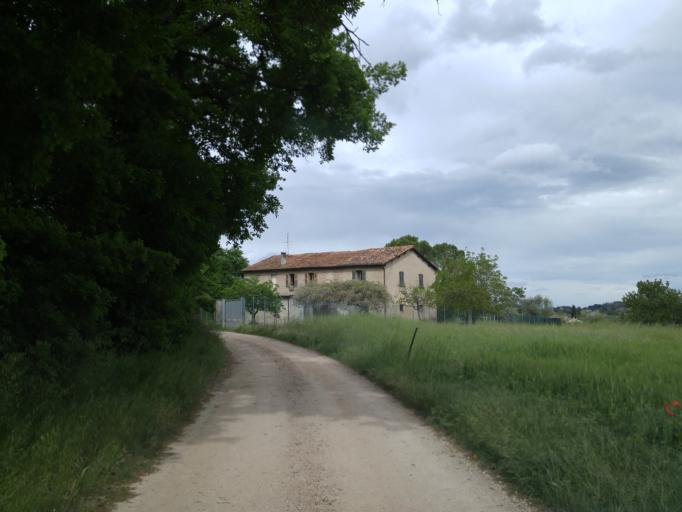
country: IT
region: The Marches
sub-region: Provincia di Pesaro e Urbino
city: Fossombrone
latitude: 43.6958
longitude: 12.8403
